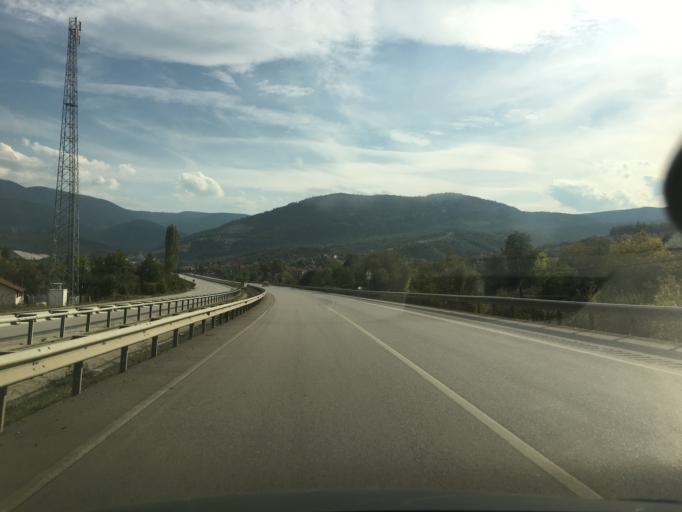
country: TR
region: Karabuk
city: Karabuk
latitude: 41.1102
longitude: 32.6689
